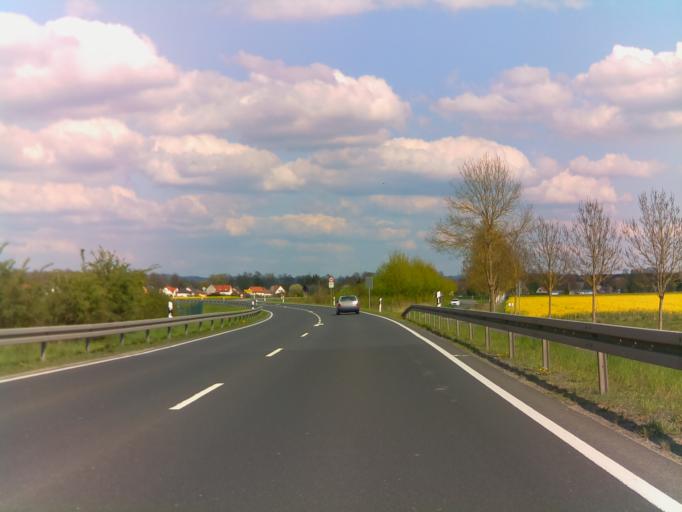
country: DE
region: Bavaria
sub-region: Upper Franconia
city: Neustadt bei Coburg
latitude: 50.3133
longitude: 11.1362
